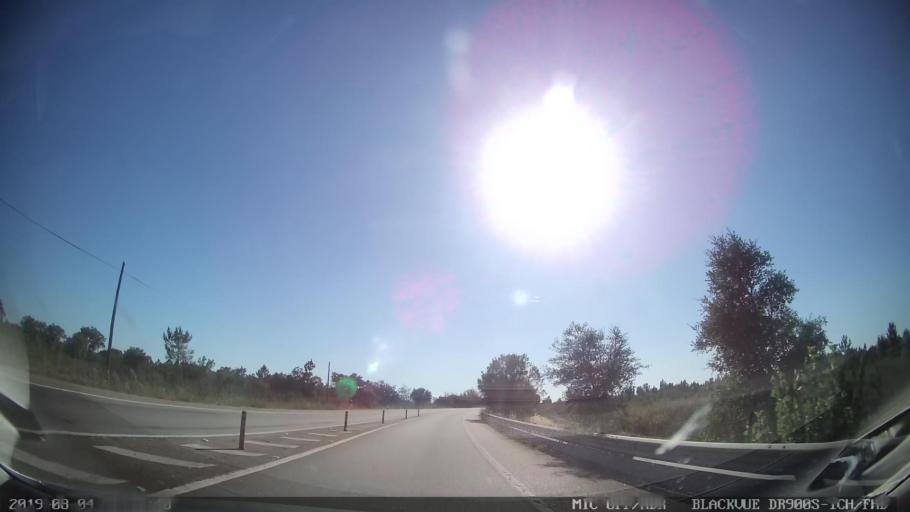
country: PT
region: Portalegre
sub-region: Gaviao
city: Gaviao
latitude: 39.4408
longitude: -7.8539
